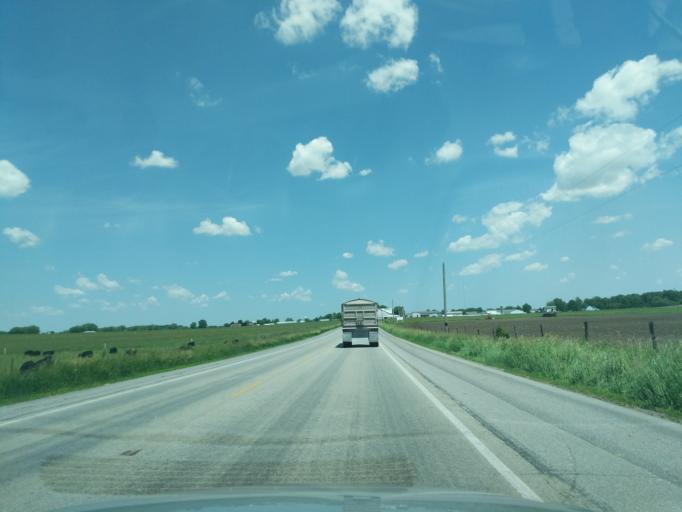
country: US
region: Indiana
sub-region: LaGrange County
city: Topeka
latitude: 41.6411
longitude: -85.5800
